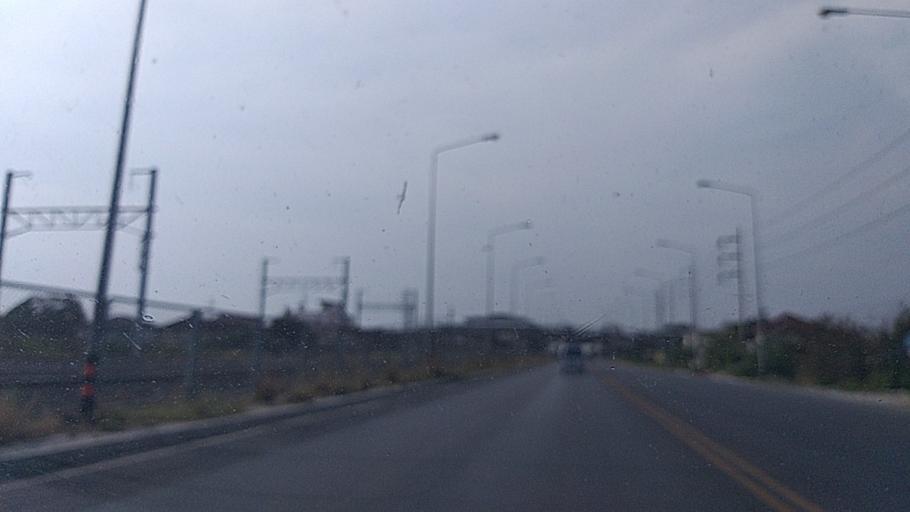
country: TH
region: Bangkok
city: Don Mueang
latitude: 13.9694
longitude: 100.6046
